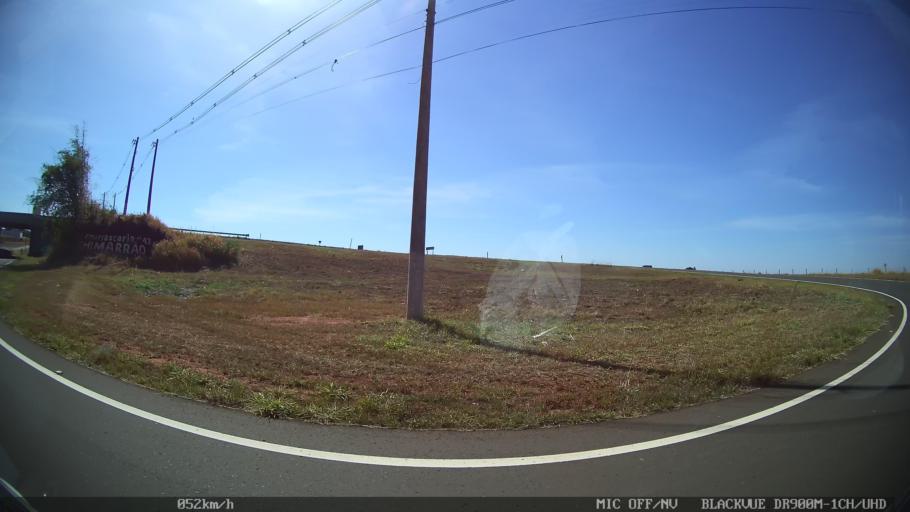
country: BR
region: Sao Paulo
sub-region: Barretos
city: Barretos
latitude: -20.5277
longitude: -48.5890
